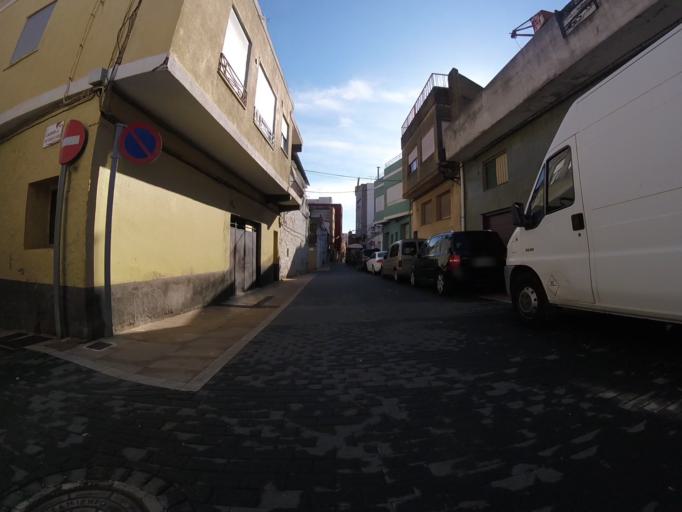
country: ES
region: Valencia
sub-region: Provincia de Castello
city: Torreblanca
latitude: 40.2219
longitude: 0.1952
